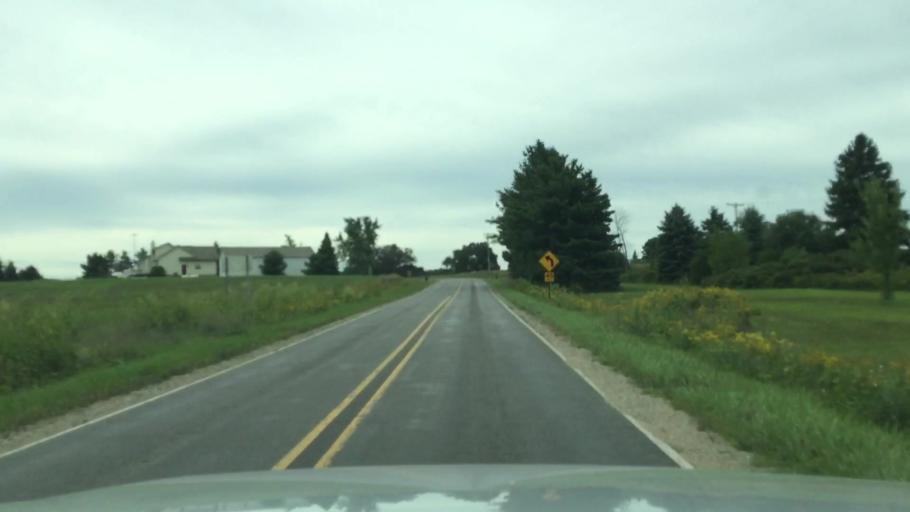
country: US
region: Michigan
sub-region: Shiawassee County
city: Durand
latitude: 42.9541
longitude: -83.9882
